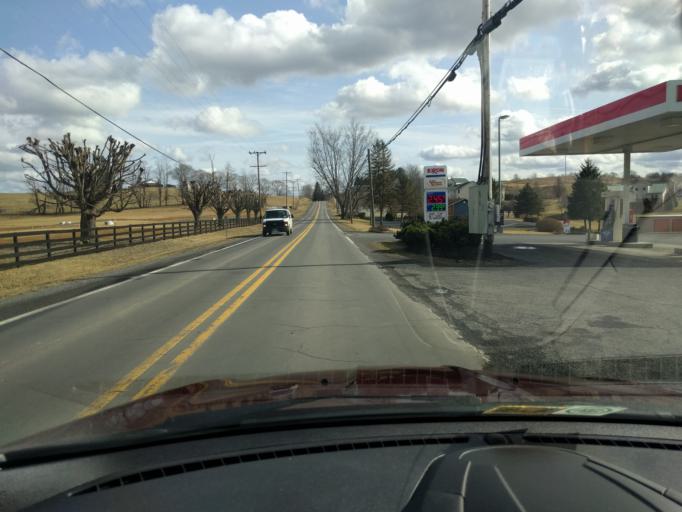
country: US
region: West Virginia
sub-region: Greenbrier County
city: Lewisburg
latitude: 37.8095
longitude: -80.4652
